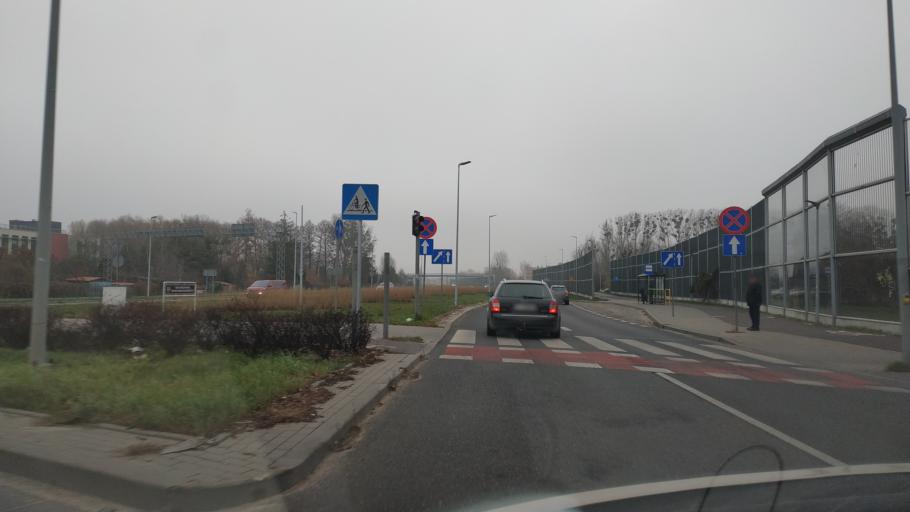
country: PL
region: Kujawsko-Pomorskie
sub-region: Torun
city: Torun
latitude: 53.0273
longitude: 18.6114
